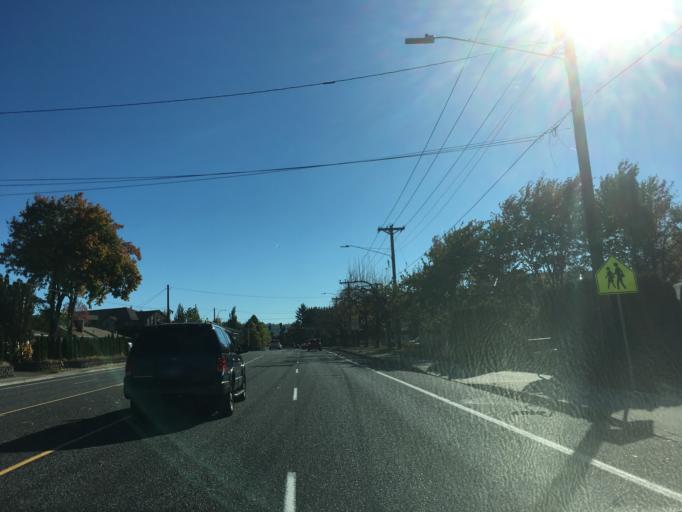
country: US
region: Oregon
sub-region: Multnomah County
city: Gresham
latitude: 45.4935
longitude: -122.3990
